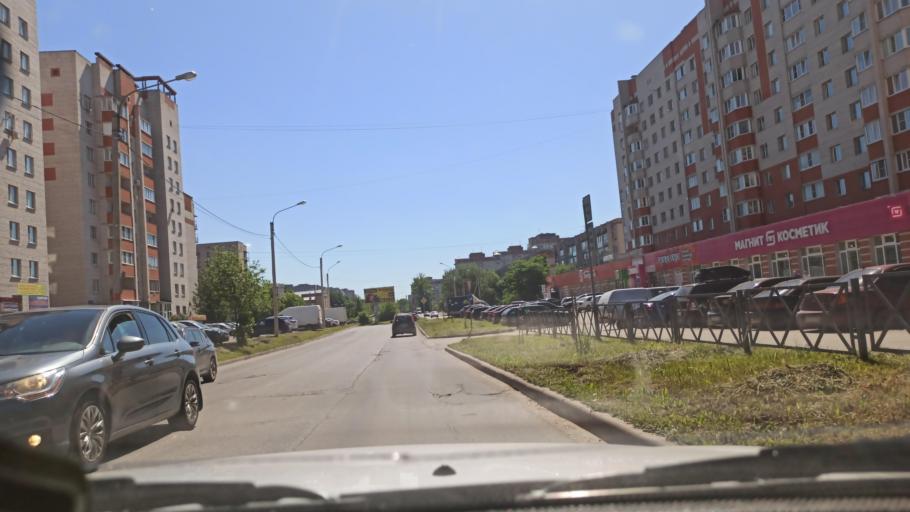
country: RU
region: Vologda
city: Vologda
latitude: 59.2090
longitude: 39.8328
